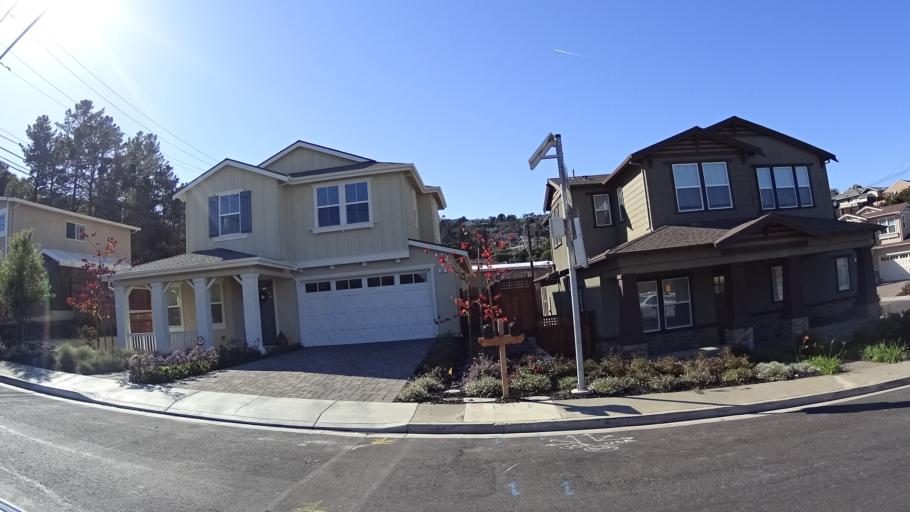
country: US
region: California
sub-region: San Mateo County
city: San Bruno
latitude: 37.6221
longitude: -122.4418
